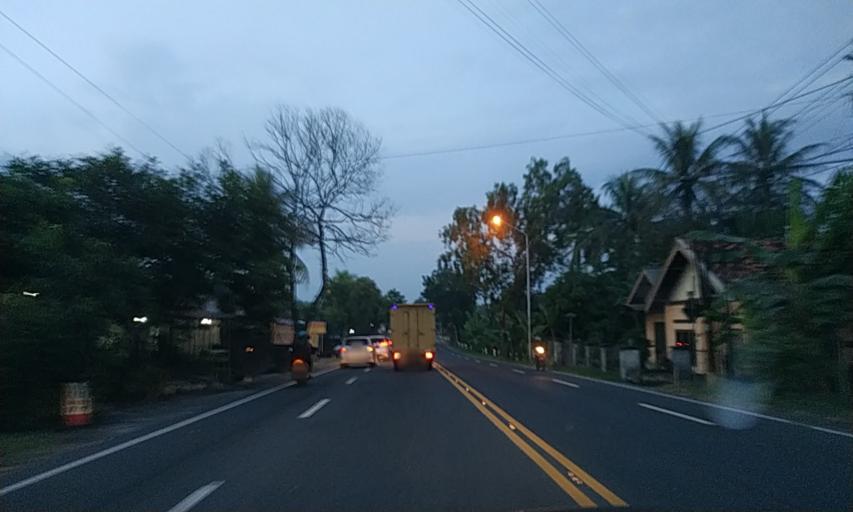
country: ID
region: Daerah Istimewa Yogyakarta
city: Godean
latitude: -7.8332
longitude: 110.2207
